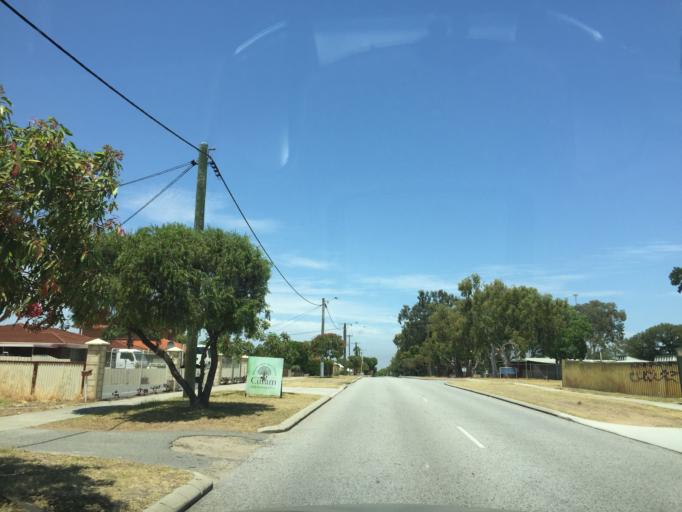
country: AU
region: Western Australia
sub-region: Canning
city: Queens Park
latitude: -31.9976
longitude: 115.9467
